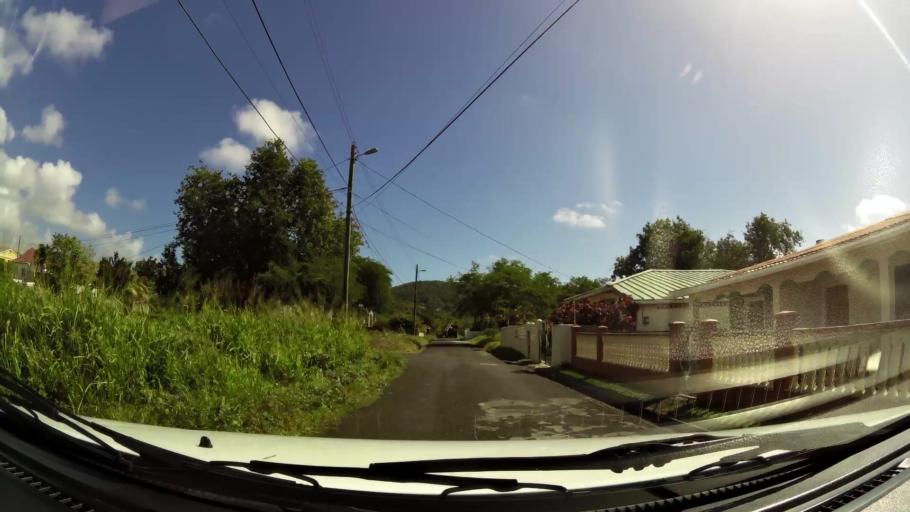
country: LC
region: Laborie Quarter
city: Laborie
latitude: 13.7429
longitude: -60.9749
